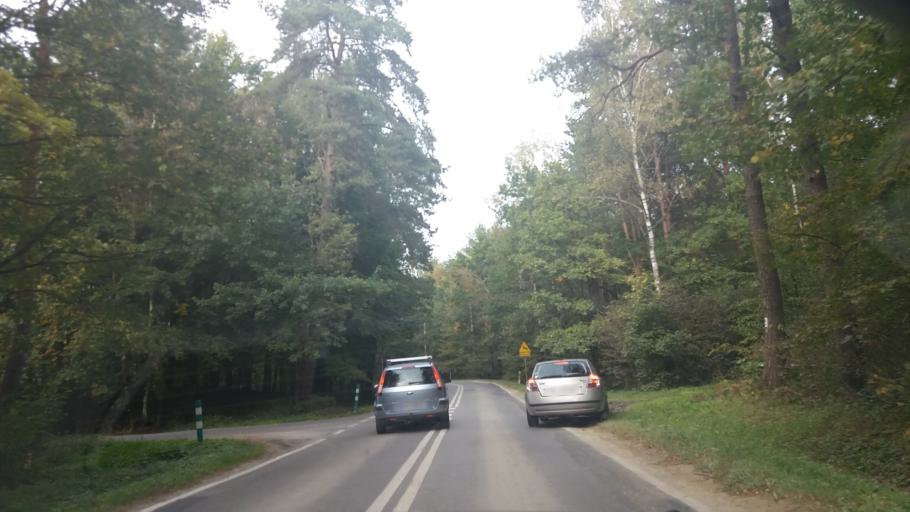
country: PL
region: Lesser Poland Voivodeship
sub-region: Powiat chrzanowski
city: Pogorzyce
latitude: 50.1153
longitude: 19.4417
